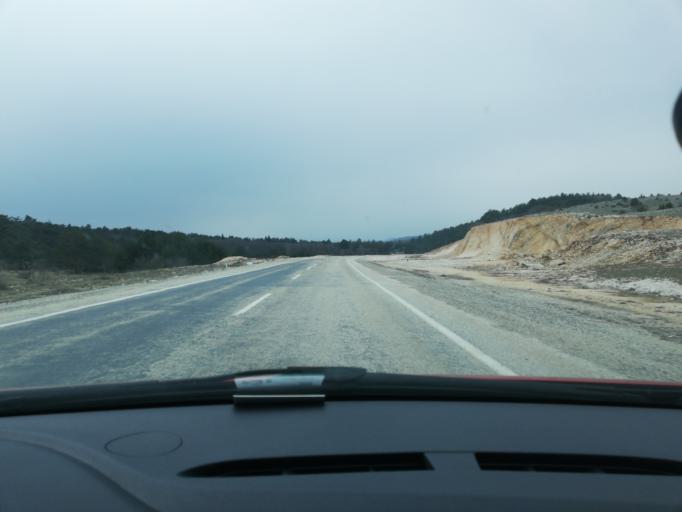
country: TR
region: Kastamonu
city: Pinarbasi
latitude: 41.5588
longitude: 33.0773
